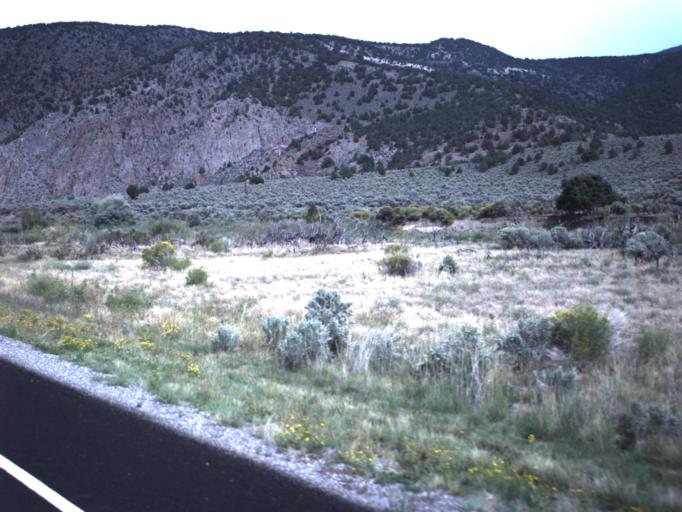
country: US
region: Utah
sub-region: Piute County
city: Junction
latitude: 38.0664
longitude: -112.3467
